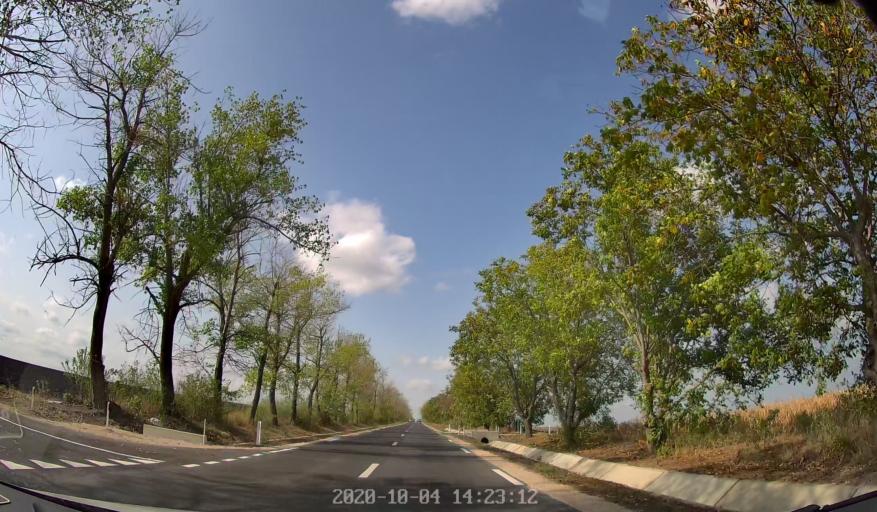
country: MD
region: Rezina
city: Saharna
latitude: 47.6061
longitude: 28.9390
